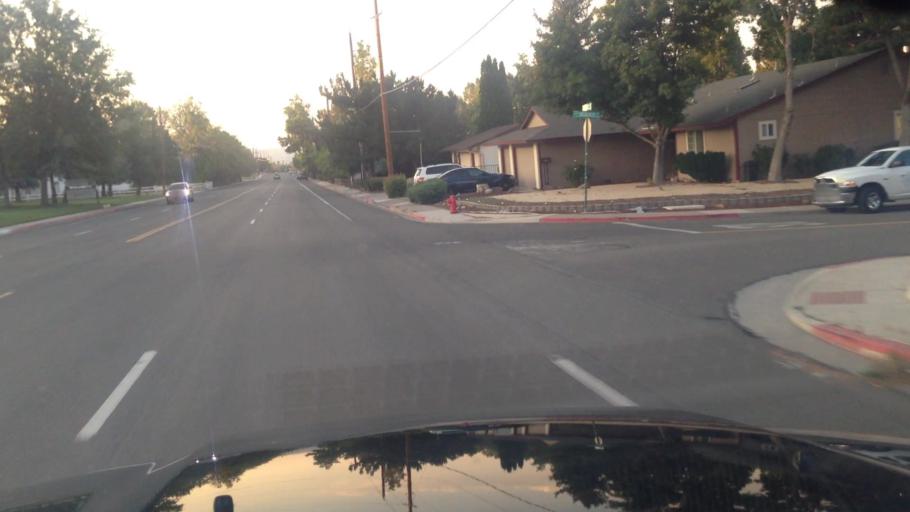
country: US
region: Nevada
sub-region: Washoe County
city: Reno
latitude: 39.4805
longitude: -119.8079
